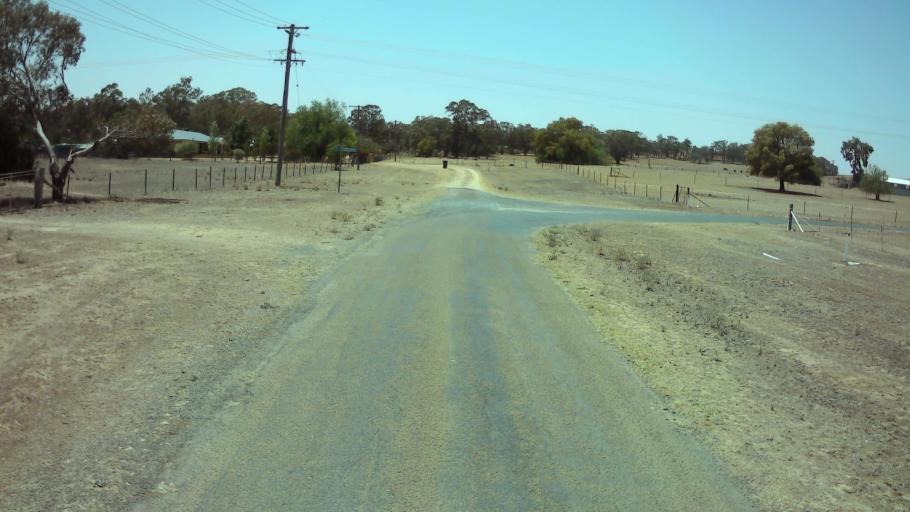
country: AU
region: New South Wales
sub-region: Weddin
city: Grenfell
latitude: -33.8919
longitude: 148.1719
